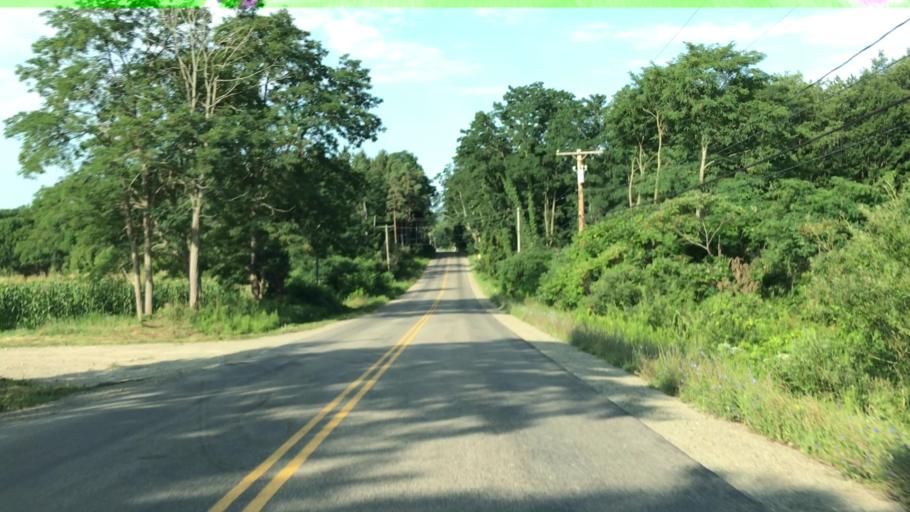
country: US
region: New York
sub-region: Chautauqua County
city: Mayville
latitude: 42.2703
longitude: -79.4658
